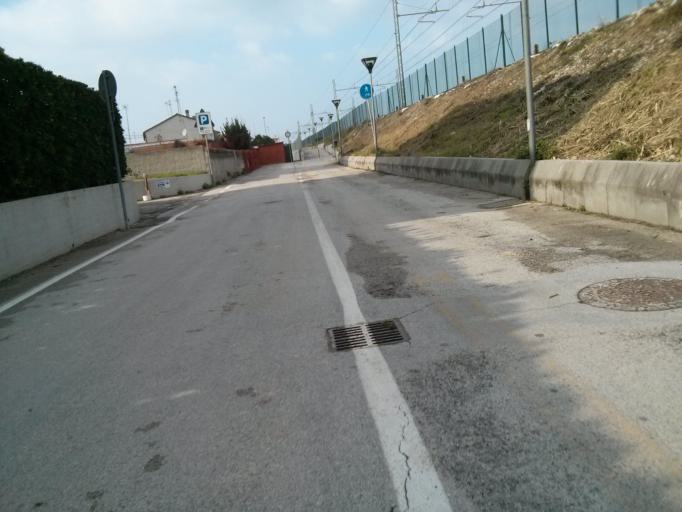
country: IT
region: The Marches
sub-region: Provincia di Pesaro e Urbino
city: Fano
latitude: 43.8532
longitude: 13.0062
